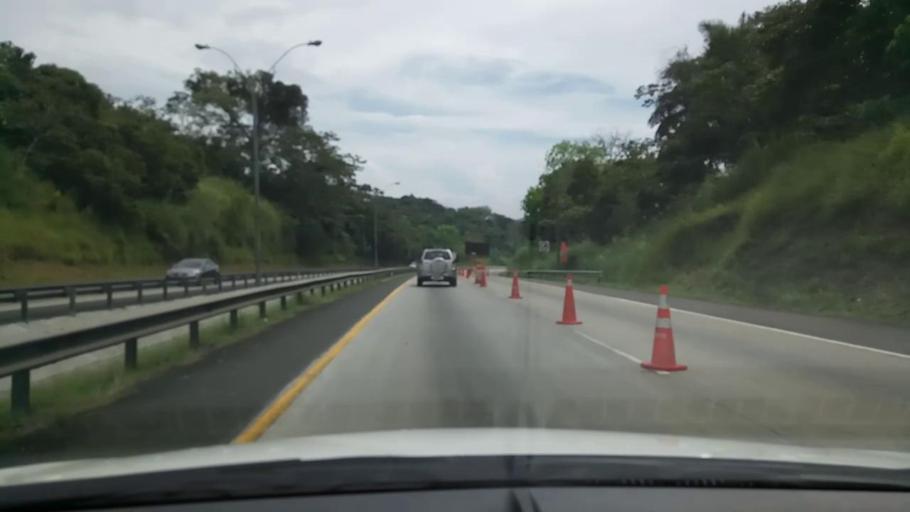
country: PA
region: Panama
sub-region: Distrito Arraijan
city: Arraijan
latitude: 8.9937
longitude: -79.6504
